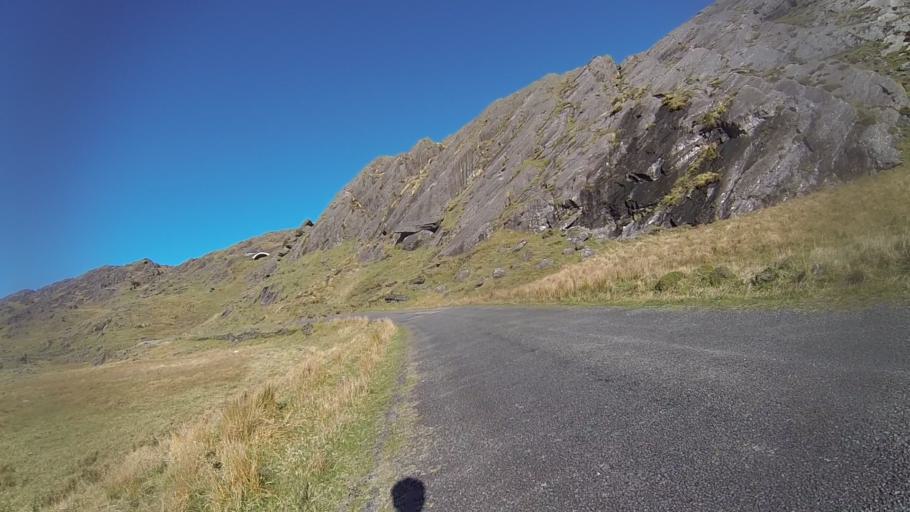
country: IE
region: Munster
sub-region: Ciarrai
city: Kenmare
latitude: 51.7208
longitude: -9.7522
